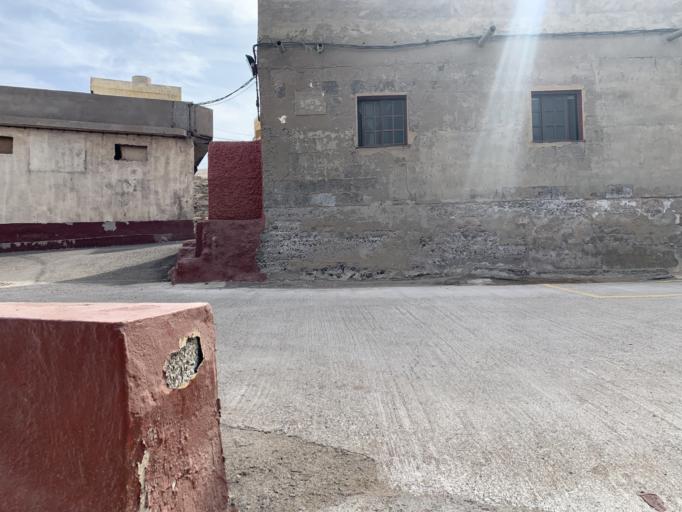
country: ES
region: Canary Islands
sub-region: Provincia de Las Palmas
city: Galdar
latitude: 28.1584
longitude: -15.6705
